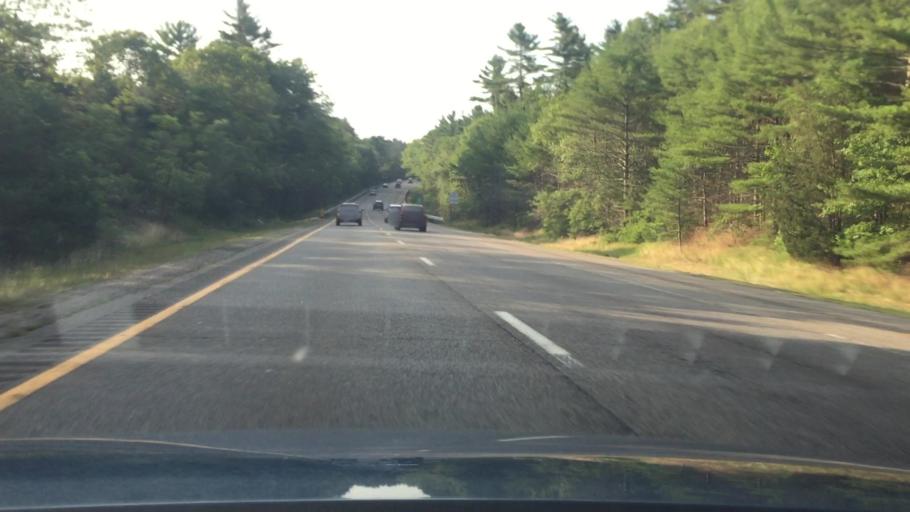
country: US
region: Massachusetts
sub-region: Plymouth County
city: North Pembroke
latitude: 42.1011
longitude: -70.7568
